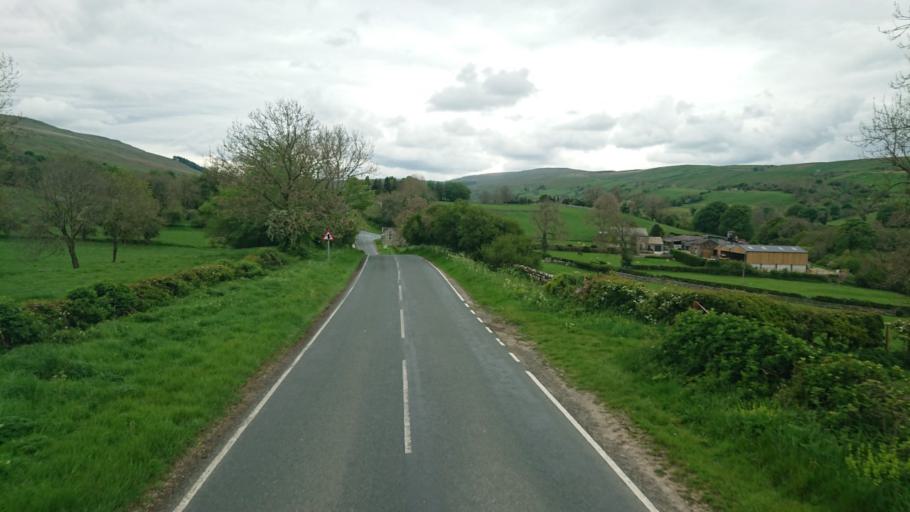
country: GB
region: England
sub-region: North Yorkshire
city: Leyburn
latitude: 54.2720
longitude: -1.9972
